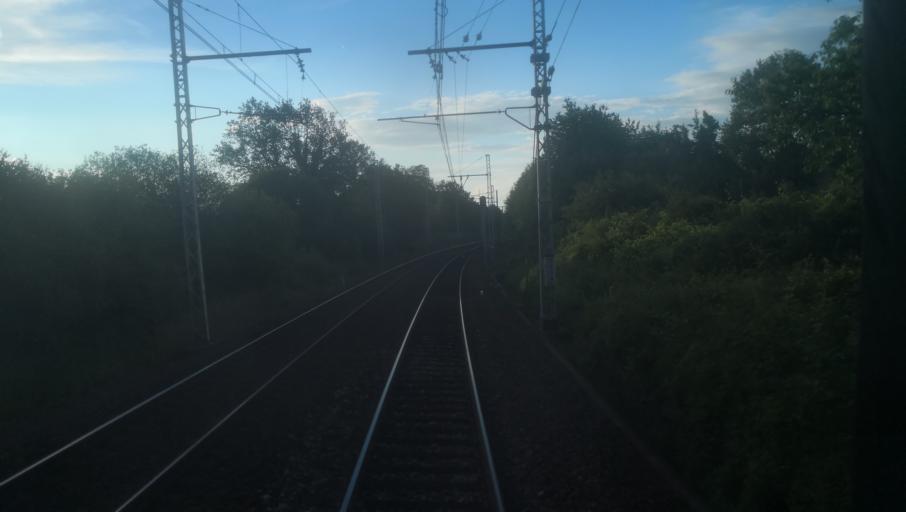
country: FR
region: Centre
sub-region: Departement de l'Indre
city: Chantome
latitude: 46.4365
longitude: 1.5526
